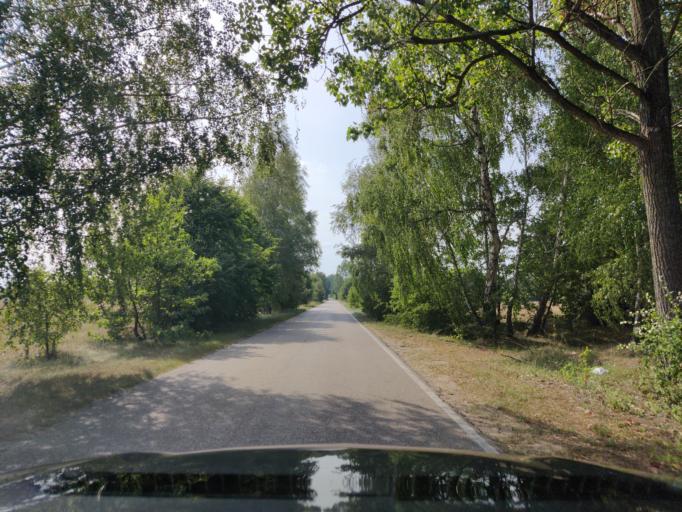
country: PL
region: Masovian Voivodeship
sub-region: Powiat wyszkowski
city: Rzasnik
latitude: 52.7652
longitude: 21.3767
